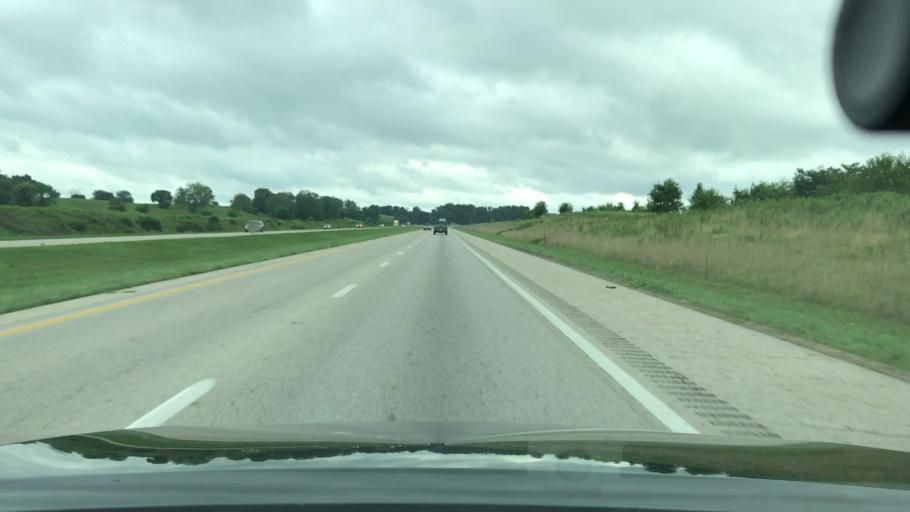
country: US
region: Ohio
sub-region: Ross County
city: Chillicothe
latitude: 39.2885
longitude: -82.8940
